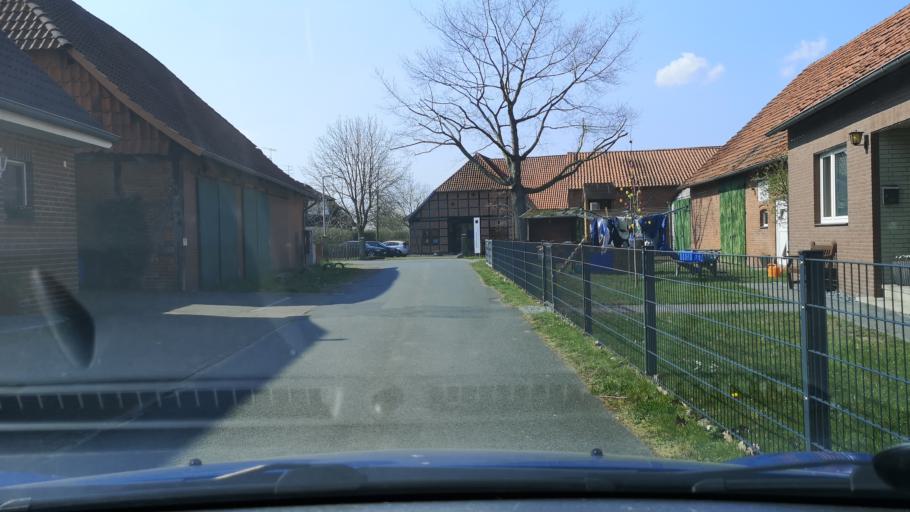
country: DE
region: Lower Saxony
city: Neustadt am Rubenberge
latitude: 52.5320
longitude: 9.4850
